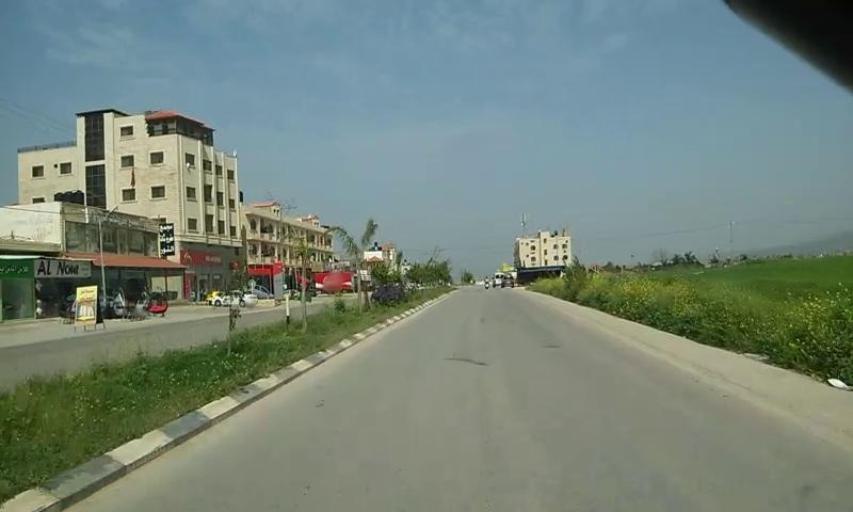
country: PS
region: West Bank
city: Al Jalamah
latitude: 32.4874
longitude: 35.2999
